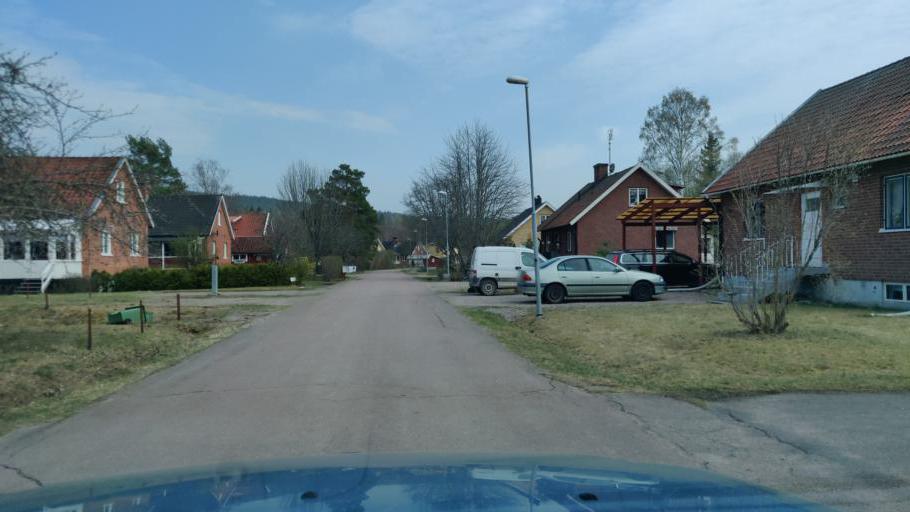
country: SE
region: Vaermland
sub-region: Munkfors Kommun
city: Munkfors
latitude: 59.8741
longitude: 13.5560
